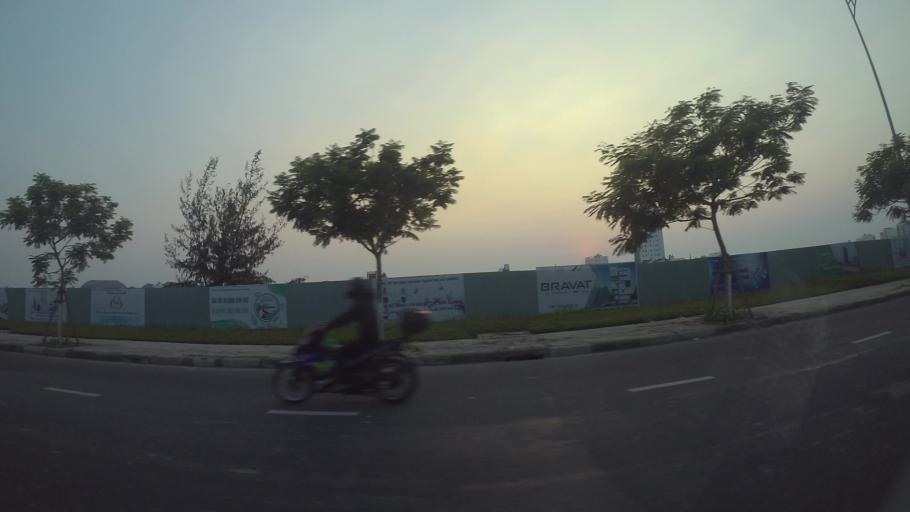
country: VN
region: Da Nang
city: Ngu Hanh Son
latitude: 16.0141
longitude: 108.2617
